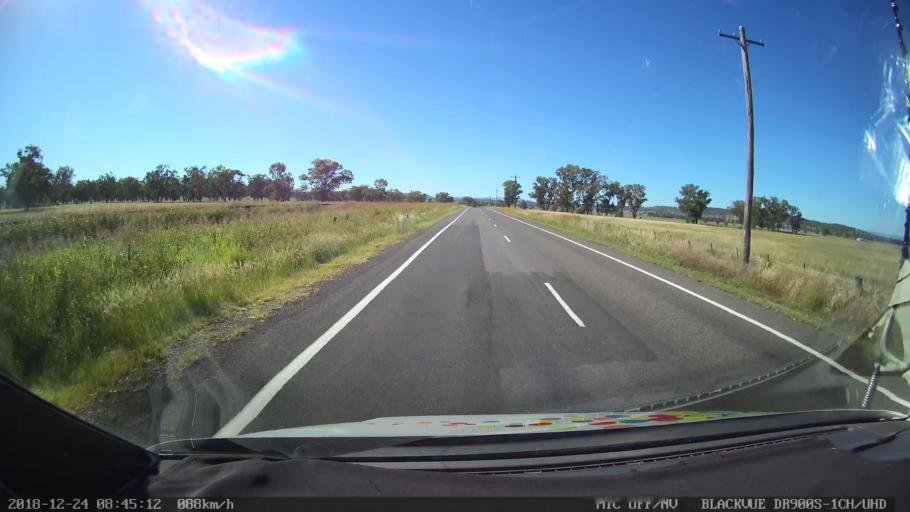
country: AU
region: New South Wales
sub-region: Liverpool Plains
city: Quirindi
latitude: -31.4118
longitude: 150.6511
